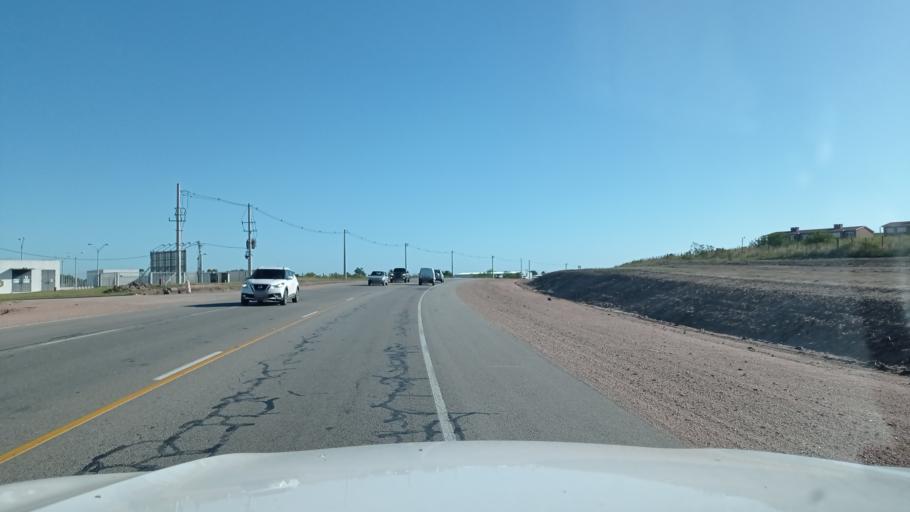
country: UY
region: Canelones
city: Pando
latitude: -34.7232
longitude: -55.9487
